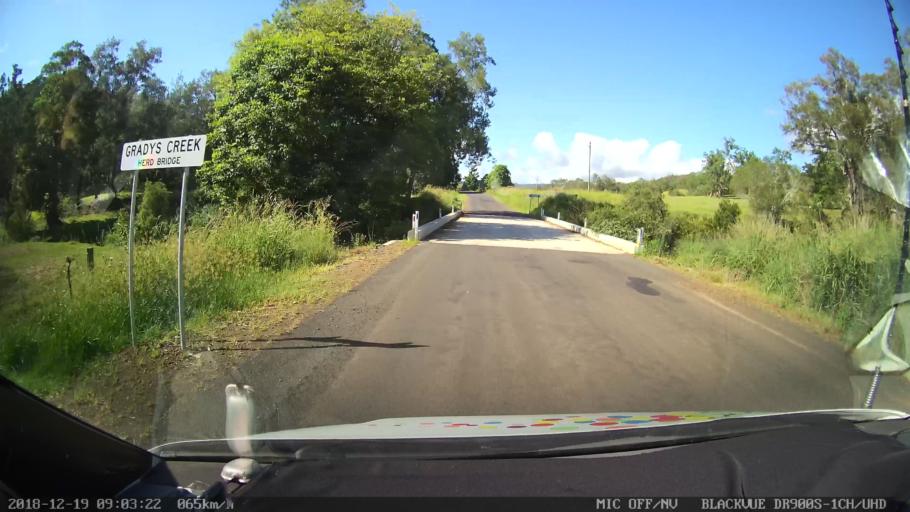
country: AU
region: New South Wales
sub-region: Kyogle
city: Kyogle
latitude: -28.4469
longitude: 152.9512
